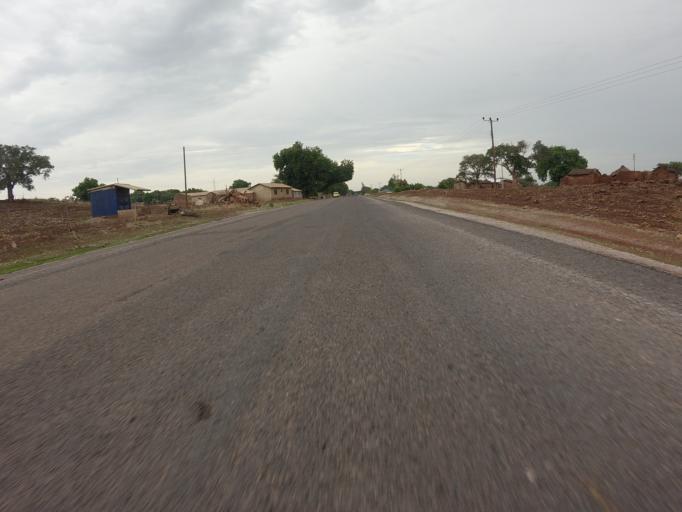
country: GH
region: Upper East
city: Bolgatanga
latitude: 10.8510
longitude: -0.6765
